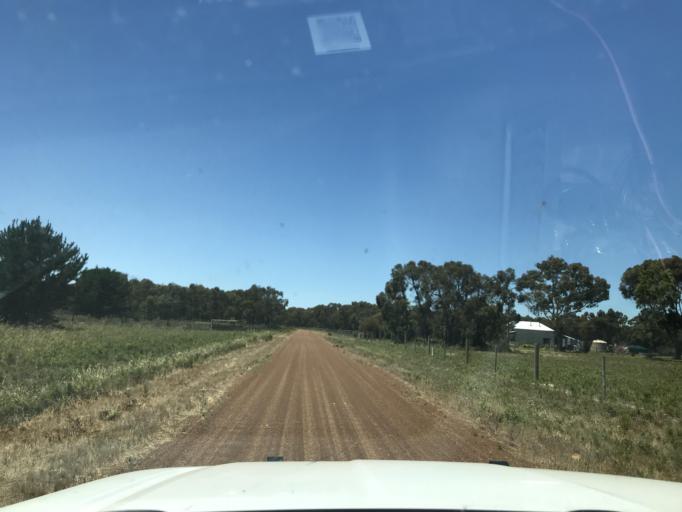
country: AU
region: South Australia
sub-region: Wattle Range
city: Penola
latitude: -37.0458
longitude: 141.3848
